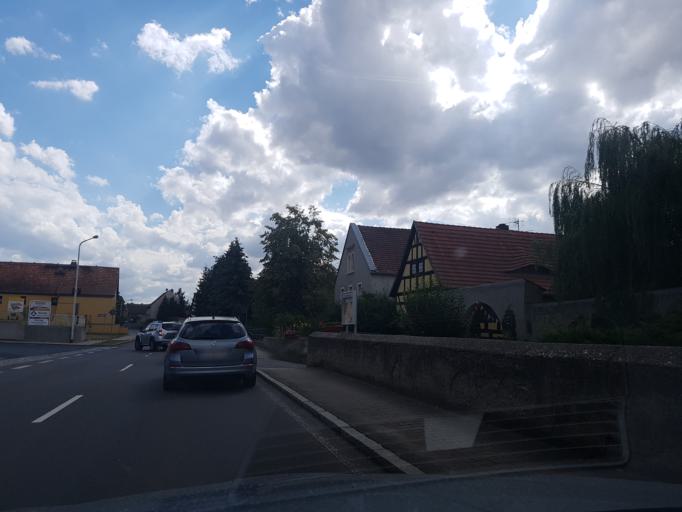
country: DE
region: Saxony
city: Priestewitz
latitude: 51.2508
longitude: 13.5479
